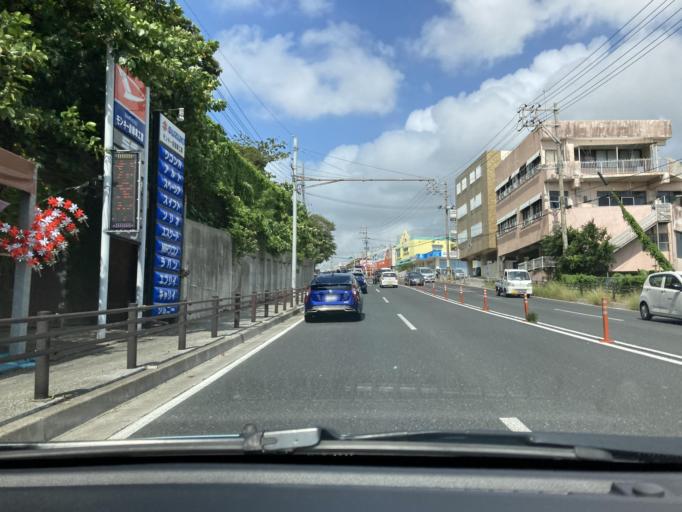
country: JP
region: Okinawa
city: Okinawa
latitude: 26.3323
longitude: 127.8214
